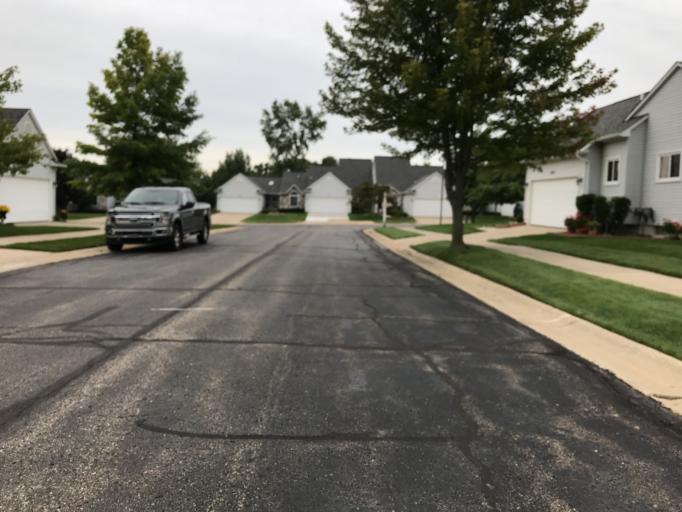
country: US
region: Michigan
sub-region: Oakland County
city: South Lyon
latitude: 42.4735
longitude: -83.6420
